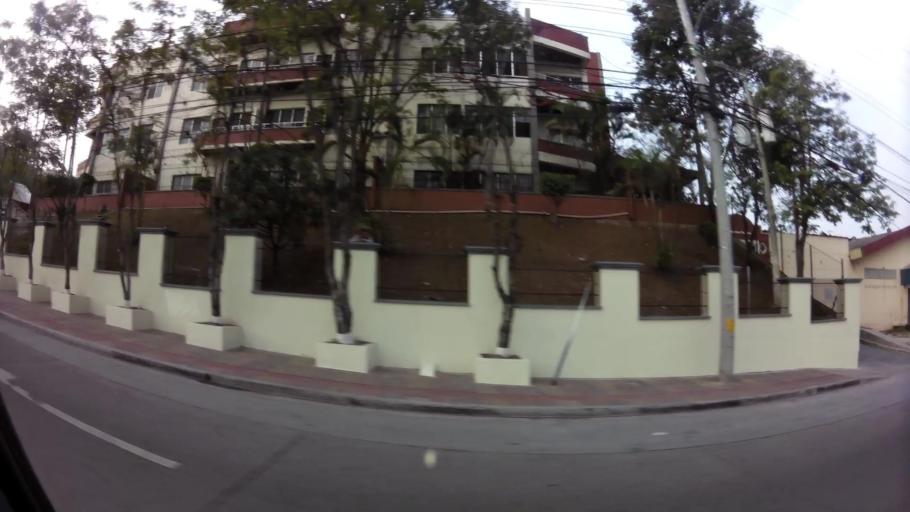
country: HN
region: Francisco Morazan
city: Tegucigalpa
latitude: 14.0849
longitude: -87.1844
